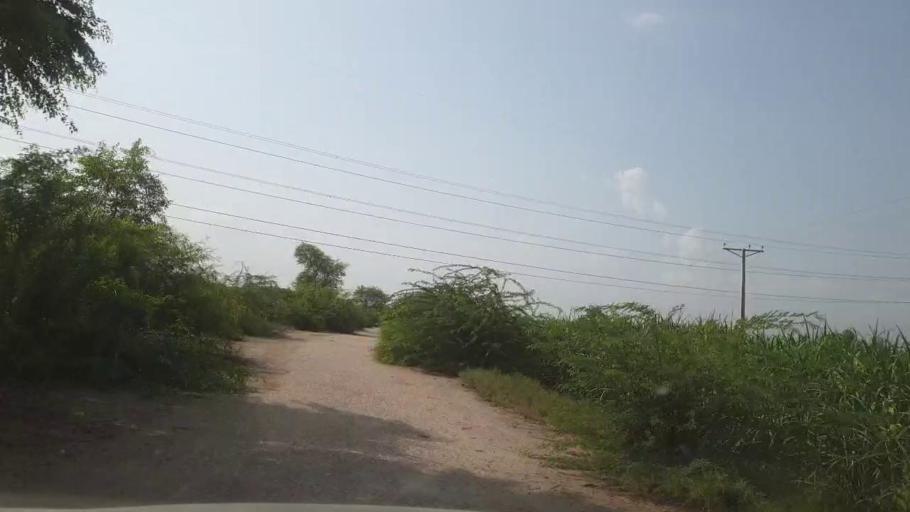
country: PK
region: Sindh
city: Pano Aqil
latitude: 27.7685
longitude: 69.1680
